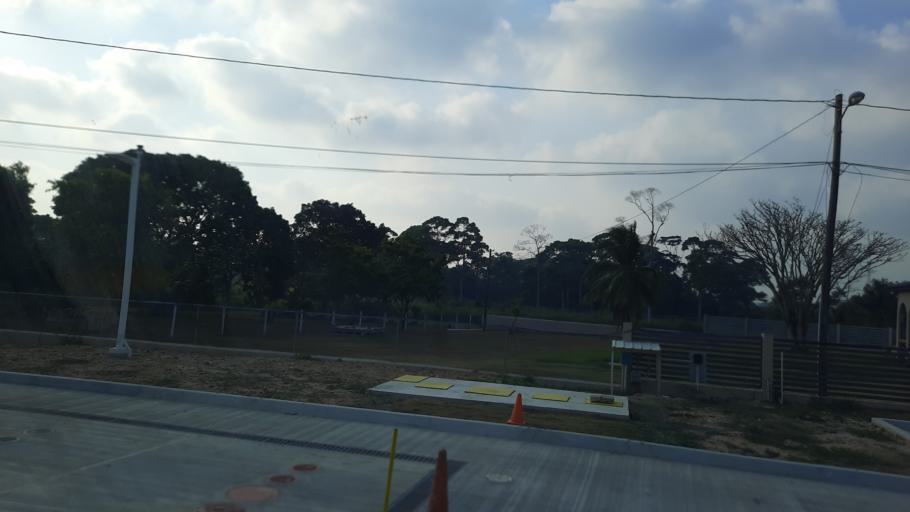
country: BZ
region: Stann Creek
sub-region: Dangriga
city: Dangriga
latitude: 16.9852
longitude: -88.2977
